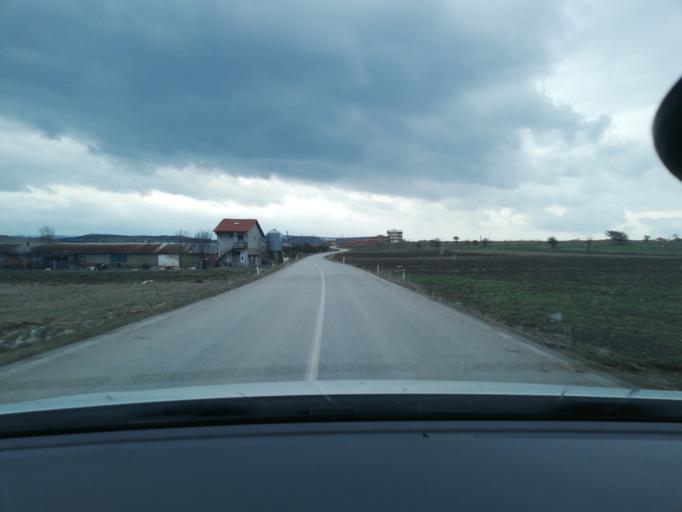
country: TR
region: Bolu
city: Gerede
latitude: 40.6945
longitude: 32.2187
